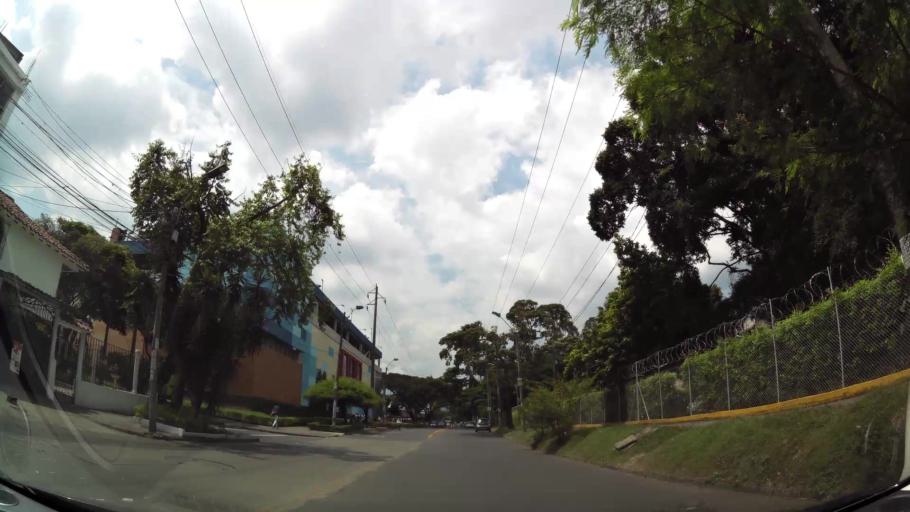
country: CO
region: Valle del Cauca
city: Cali
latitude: 3.4662
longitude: -76.4995
